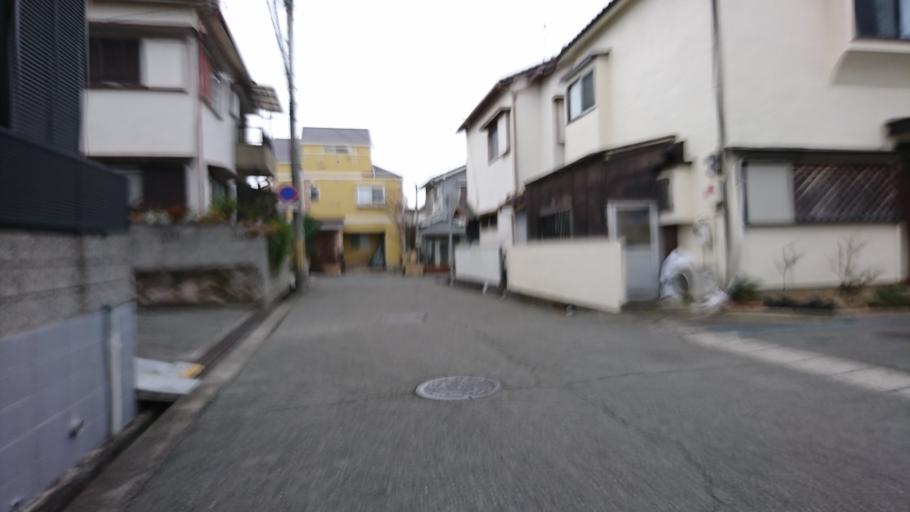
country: JP
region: Hyogo
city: Kakogawacho-honmachi
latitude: 34.7412
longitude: 134.8689
